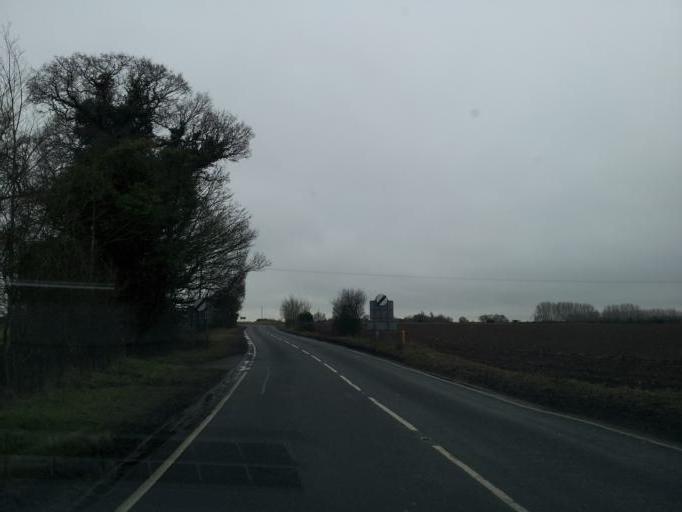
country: GB
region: England
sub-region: Essex
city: Manningtree
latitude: 51.9369
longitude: 1.0625
